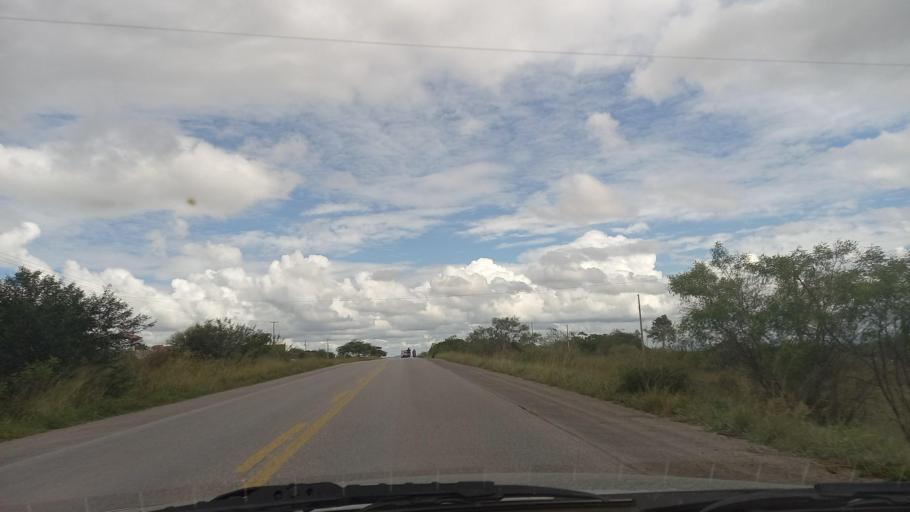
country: BR
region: Pernambuco
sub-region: Cachoeirinha
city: Cachoeirinha
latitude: -8.3704
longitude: -36.1726
